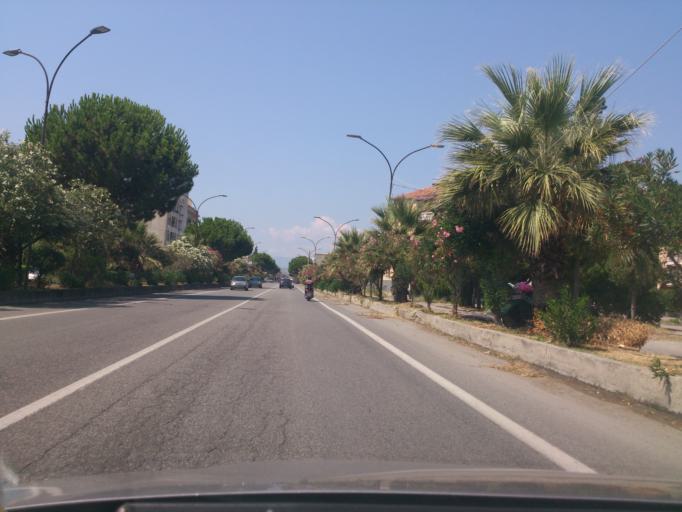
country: IT
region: Calabria
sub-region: Provincia di Reggio Calabria
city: Marina di Gioiosa Ionica
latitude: 38.3051
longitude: 16.3385
